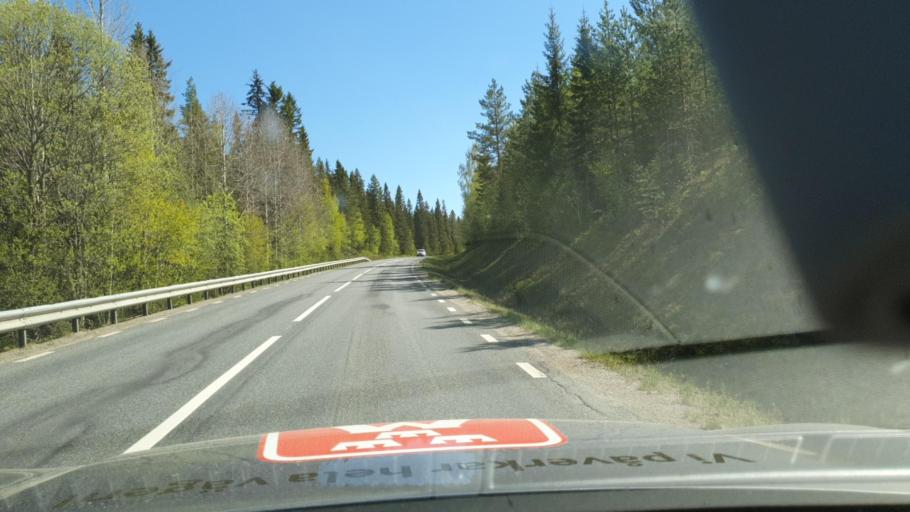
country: SE
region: Vaesternorrland
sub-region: OErnskoeldsviks Kommun
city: Ornskoldsvik
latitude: 63.6934
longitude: 18.5177
